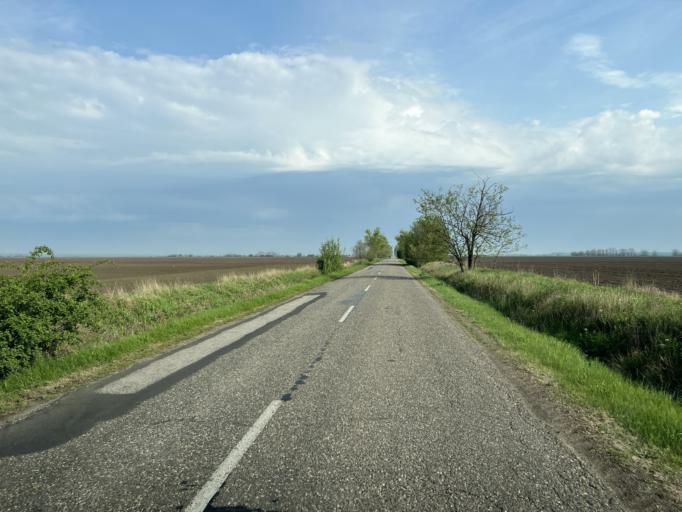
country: HU
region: Pest
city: Tapioszentmarton
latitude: 47.2720
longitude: 19.7685
